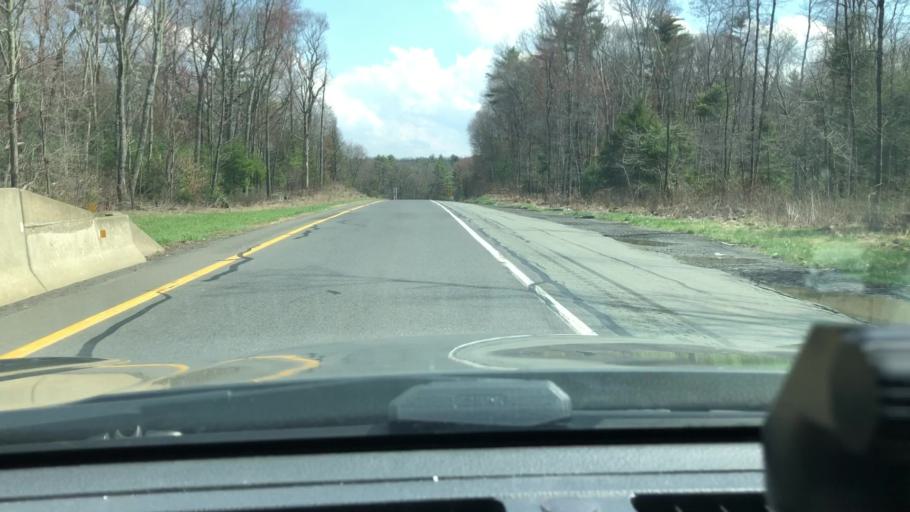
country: US
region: Pennsylvania
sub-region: Monroe County
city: Tannersville
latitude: 40.9967
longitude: -75.2718
